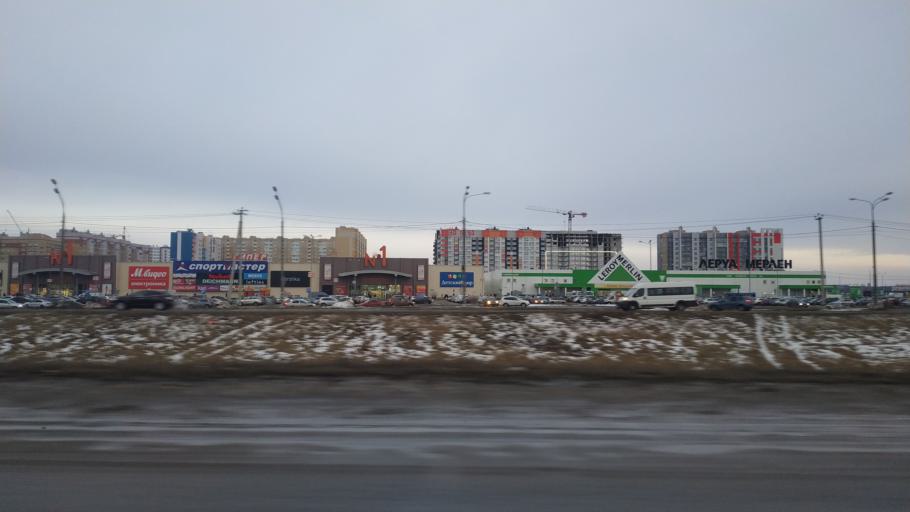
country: RU
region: Tverskaya
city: Tver
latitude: 56.8156
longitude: 35.8804
